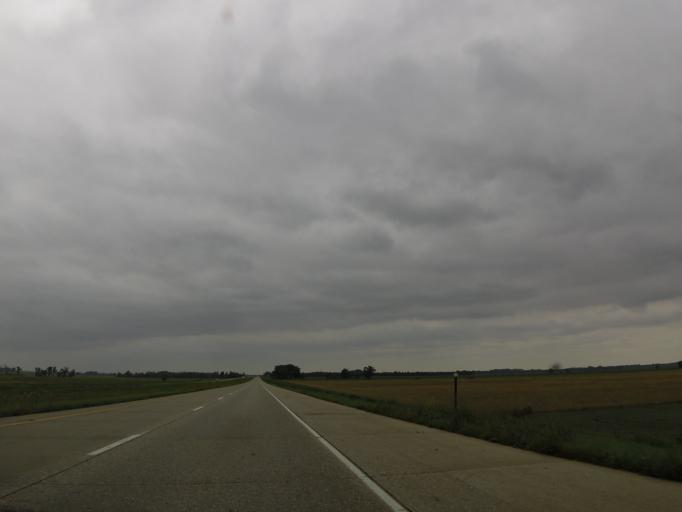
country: US
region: South Dakota
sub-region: Roberts County
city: Sisseton
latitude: 45.5938
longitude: -96.9893
